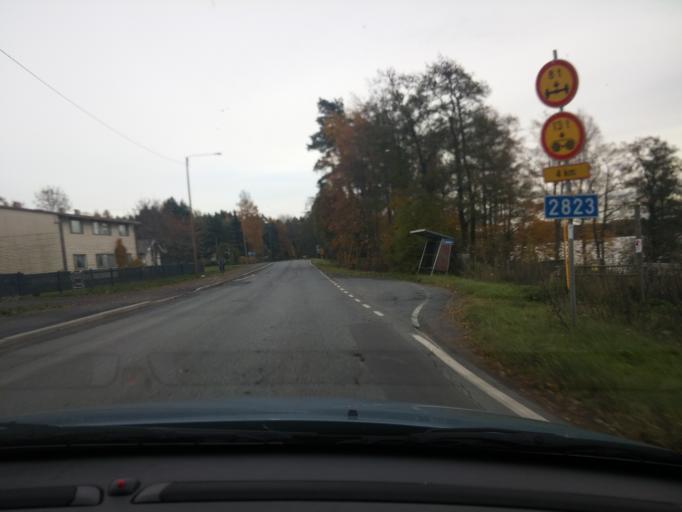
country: FI
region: Haeme
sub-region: Forssa
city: Tammela
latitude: 60.8059
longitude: 23.7962
